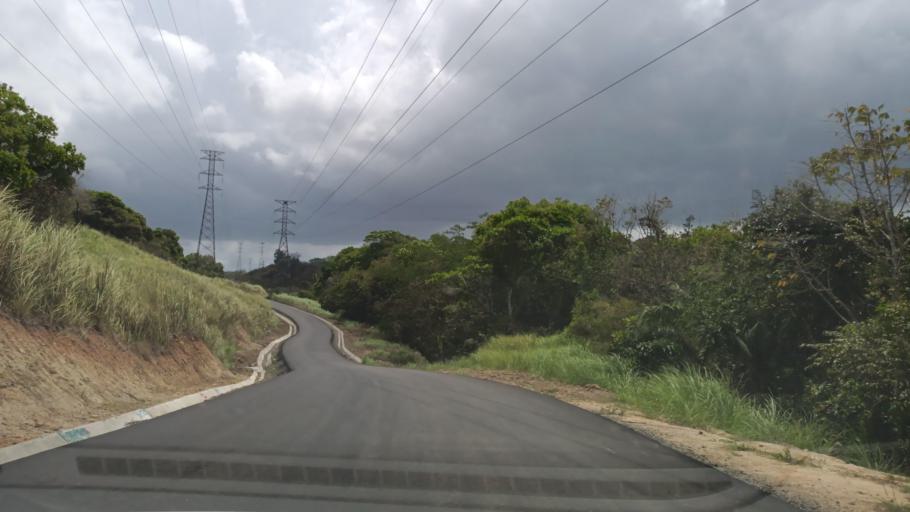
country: PA
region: Panama
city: Alcalde Diaz
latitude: 9.0836
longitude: -79.5781
